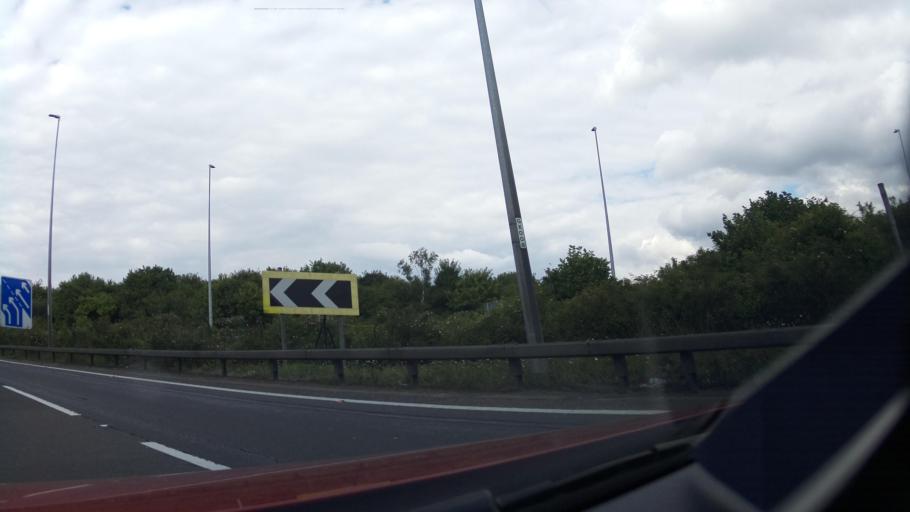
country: GB
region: England
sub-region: Hertfordshire
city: Abbots Langley
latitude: 51.7172
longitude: -0.3874
